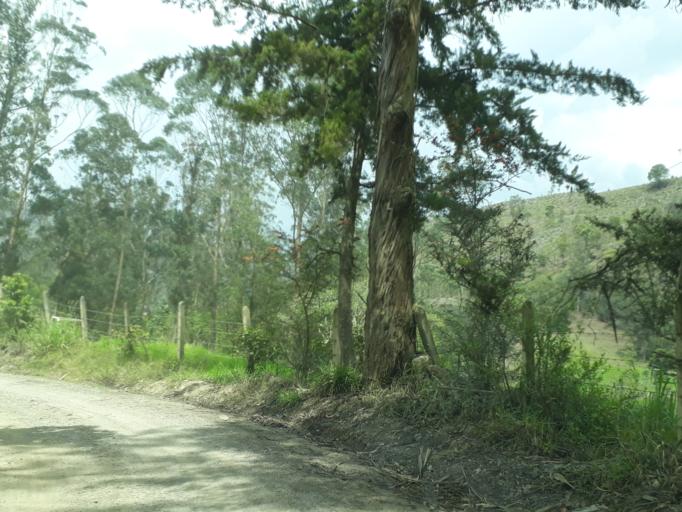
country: CO
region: Cundinamarca
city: Macheta
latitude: 5.0841
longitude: -73.5763
